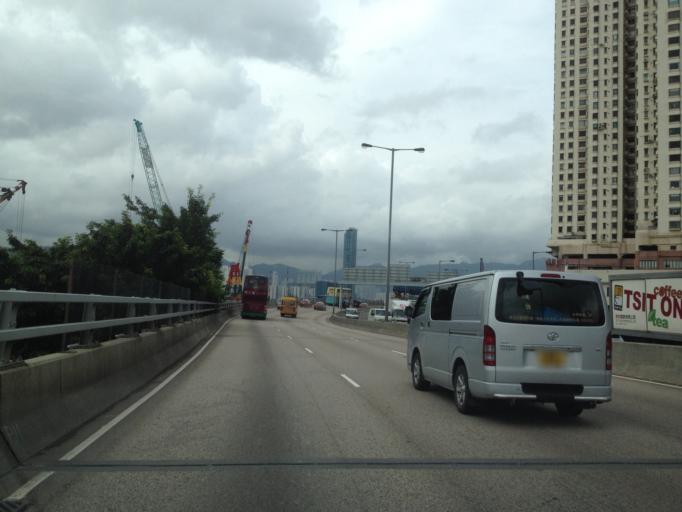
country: HK
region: Wanchai
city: Wan Chai
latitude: 22.2860
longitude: 114.1892
